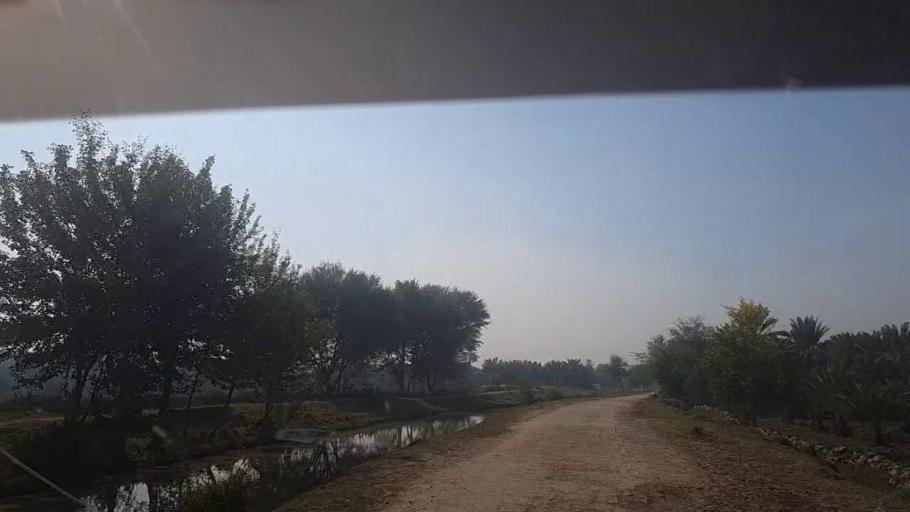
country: PK
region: Sindh
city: Khairpur
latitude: 27.4741
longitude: 68.7274
